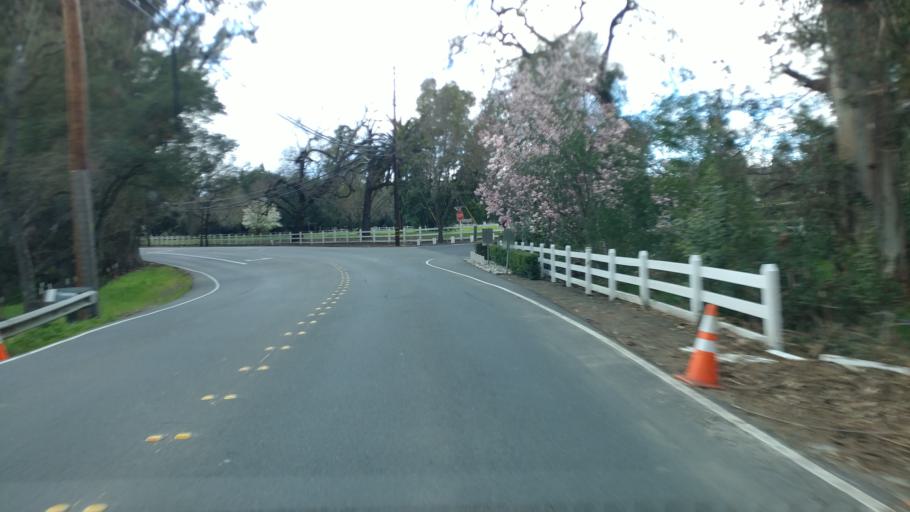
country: US
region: California
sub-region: Contra Costa County
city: Diablo
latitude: 37.8348
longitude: -121.9667
